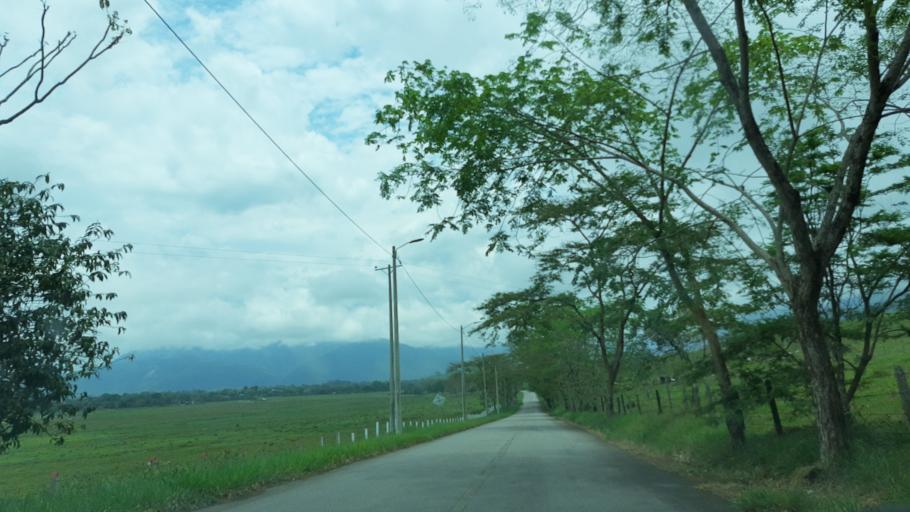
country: CO
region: Casanare
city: Sabanalarga
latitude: 4.8394
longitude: -73.0416
